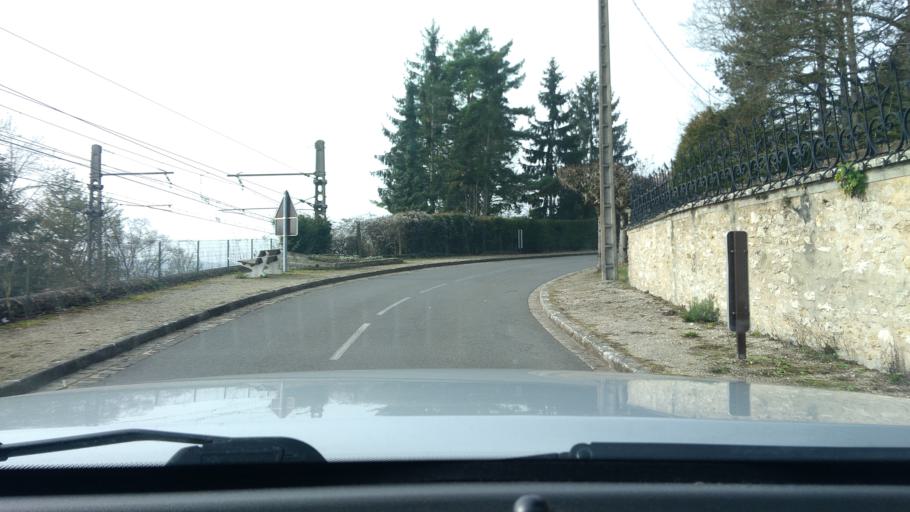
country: FR
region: Ile-de-France
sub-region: Departement de Seine-et-Marne
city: Chartrettes
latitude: 48.4863
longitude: 2.7099
